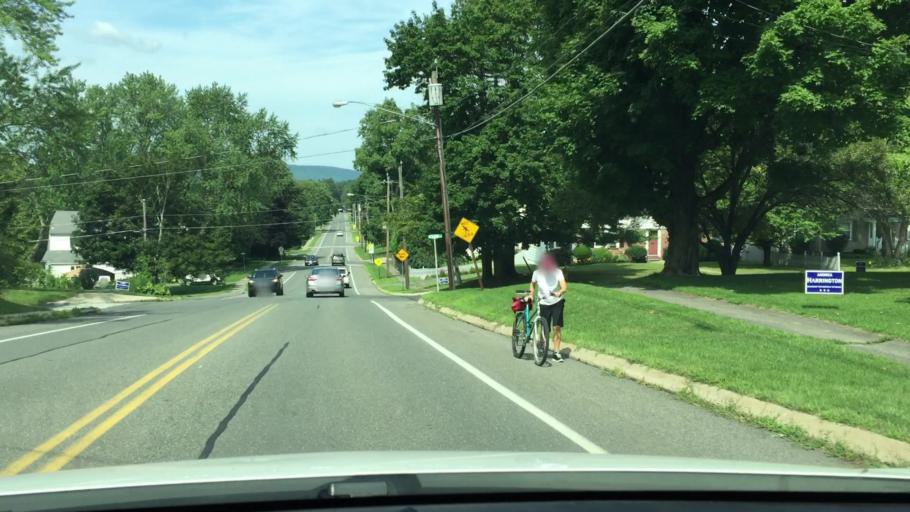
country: US
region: Massachusetts
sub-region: Berkshire County
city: Pittsfield
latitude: 42.4361
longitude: -73.2375
